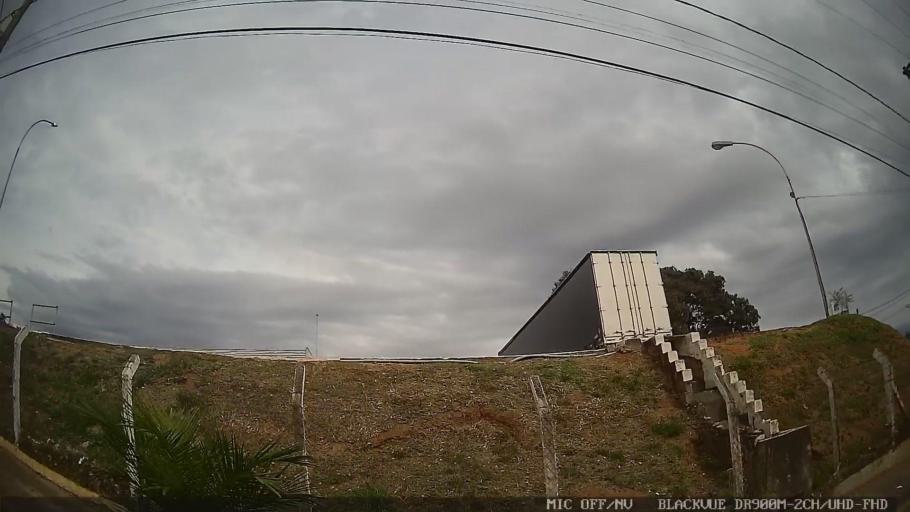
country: BR
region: Sao Paulo
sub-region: Salto
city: Salto
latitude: -23.1914
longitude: -47.2818
